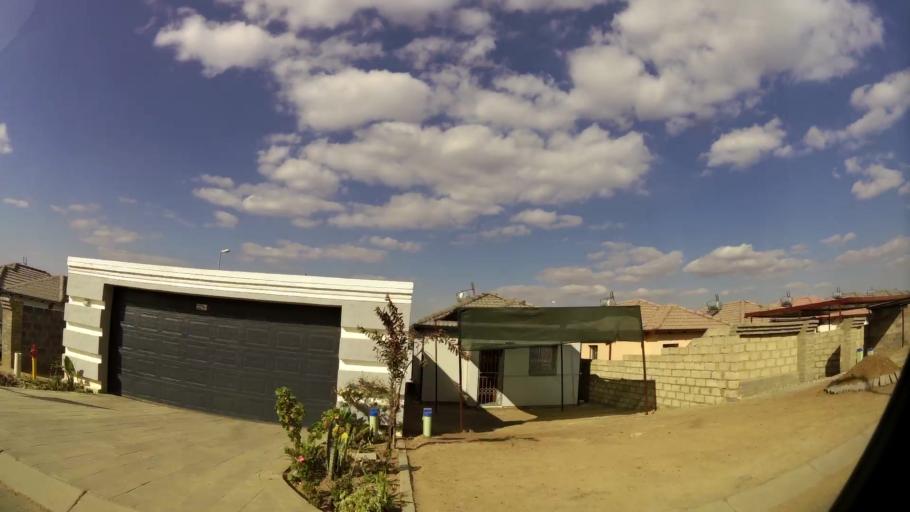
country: ZA
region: Gauteng
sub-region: Ekurhuleni Metropolitan Municipality
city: Tembisa
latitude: -25.9818
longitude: 28.1906
